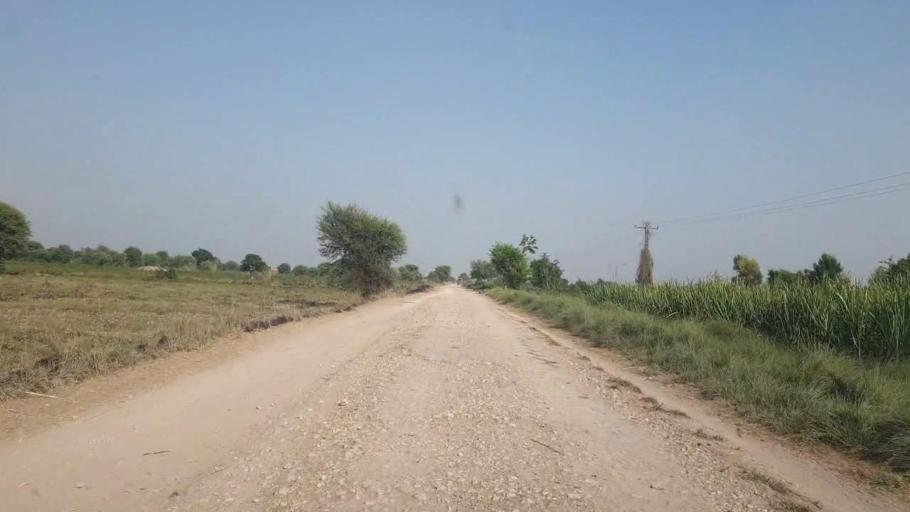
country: PK
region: Sindh
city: Sinjhoro
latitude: 26.0559
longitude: 68.8537
